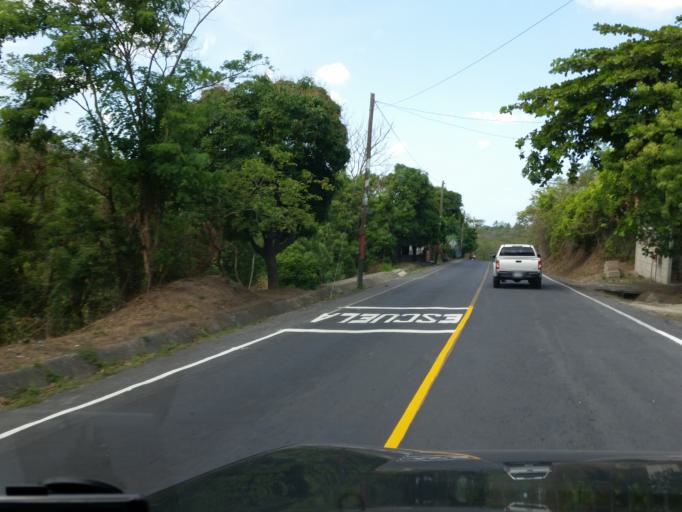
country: NI
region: Masaya
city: La Concepcion
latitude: 11.9584
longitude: -86.1936
